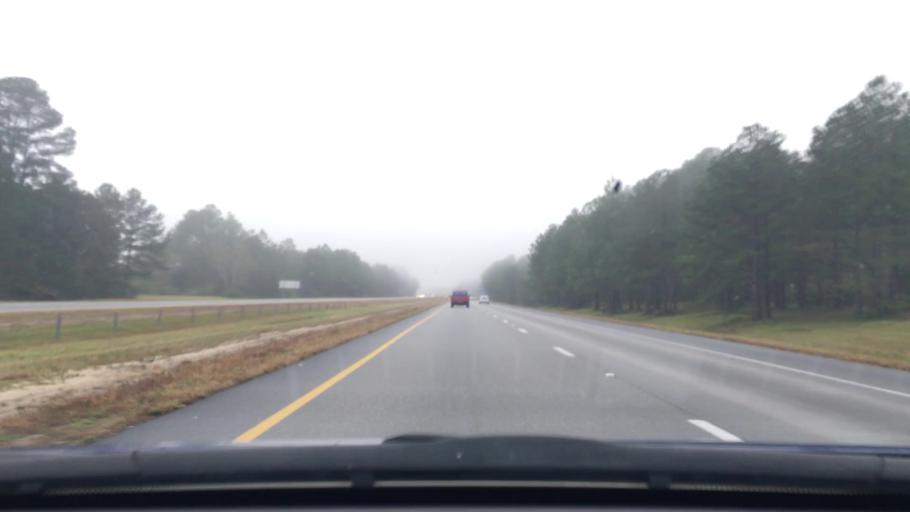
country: US
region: South Carolina
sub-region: Lee County
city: Bishopville
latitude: 34.2102
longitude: -80.4035
